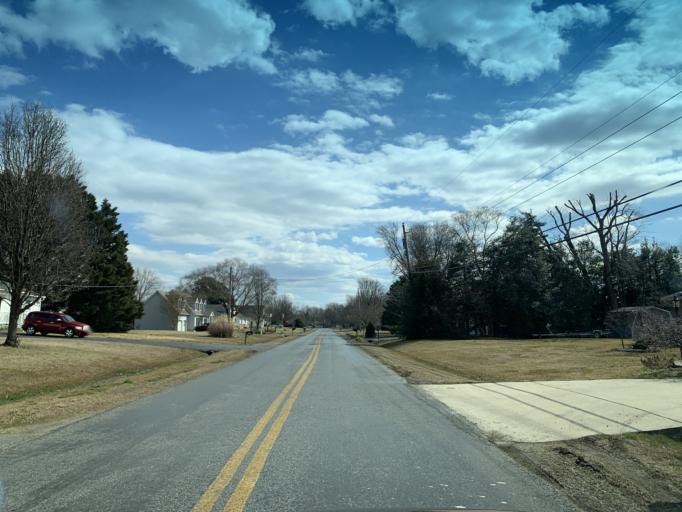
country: US
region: Maryland
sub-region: Queen Anne's County
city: Chester
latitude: 38.9323
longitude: -76.2653
